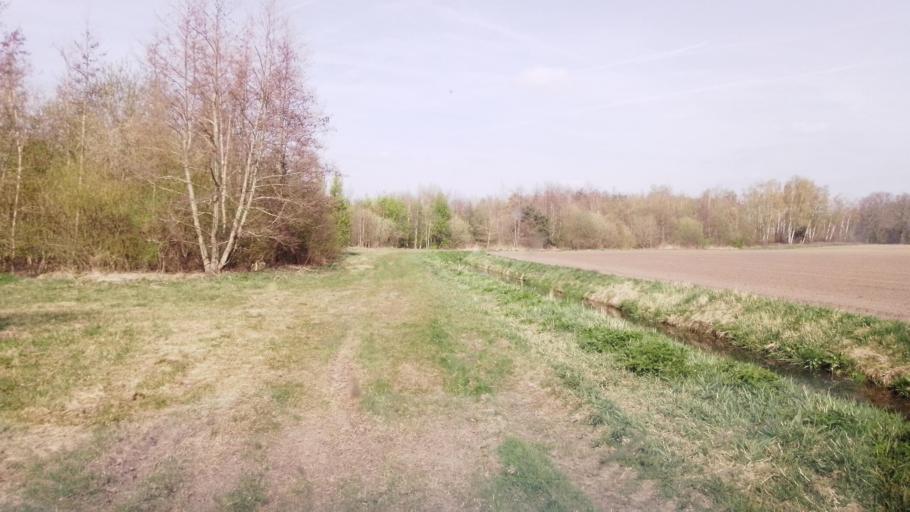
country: NL
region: Limburg
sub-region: Gemeente Peel en Maas
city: Maasbree
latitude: 51.3820
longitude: 6.0793
